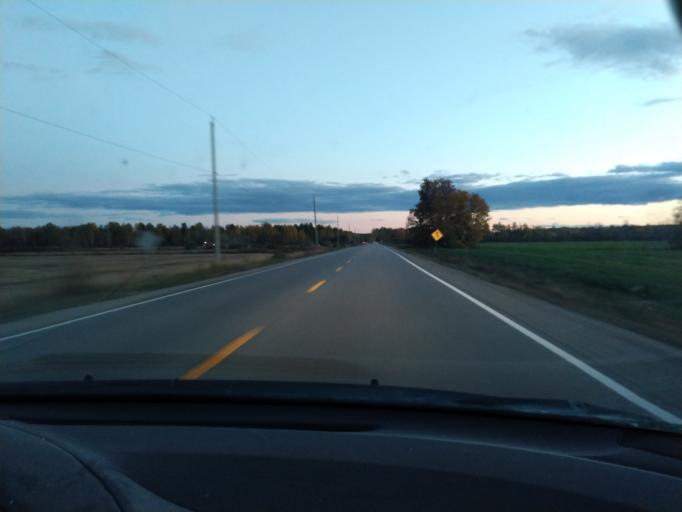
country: CA
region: Ontario
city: Bradford West Gwillimbury
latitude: 44.1940
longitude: -79.6633
